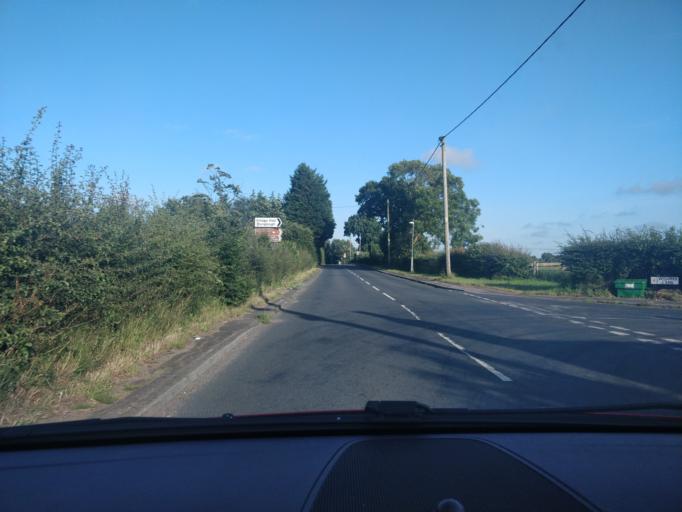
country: GB
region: England
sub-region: Lancashire
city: Tarleton
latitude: 53.6465
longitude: -2.8666
